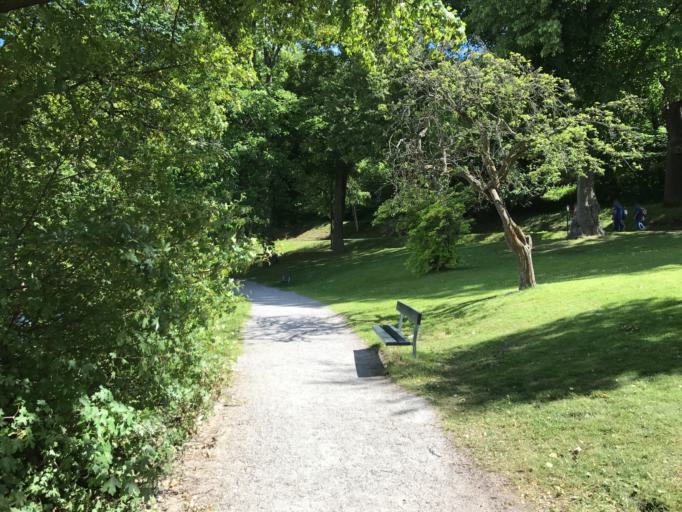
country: SE
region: Stockholm
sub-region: Stockholms Kommun
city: OEstermalm
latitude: 59.3292
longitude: 18.1030
